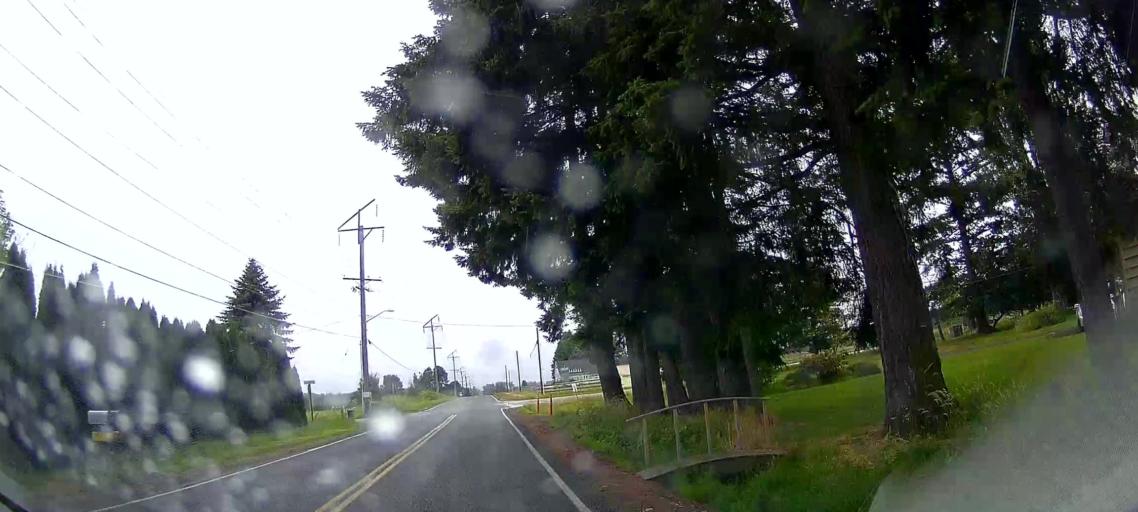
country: US
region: Washington
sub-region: Whatcom County
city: Birch Bay
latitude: 48.8846
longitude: -122.7043
